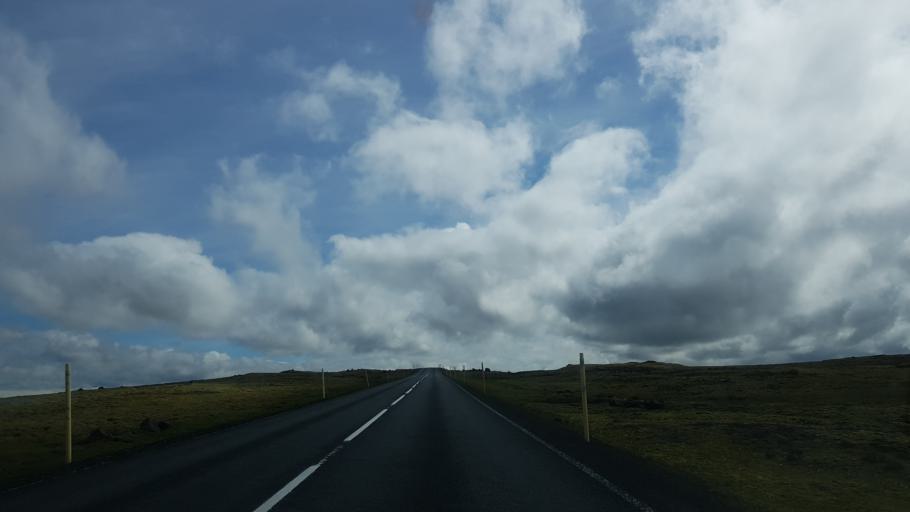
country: IS
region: West
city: Borgarnes
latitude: 64.9957
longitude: -21.0653
